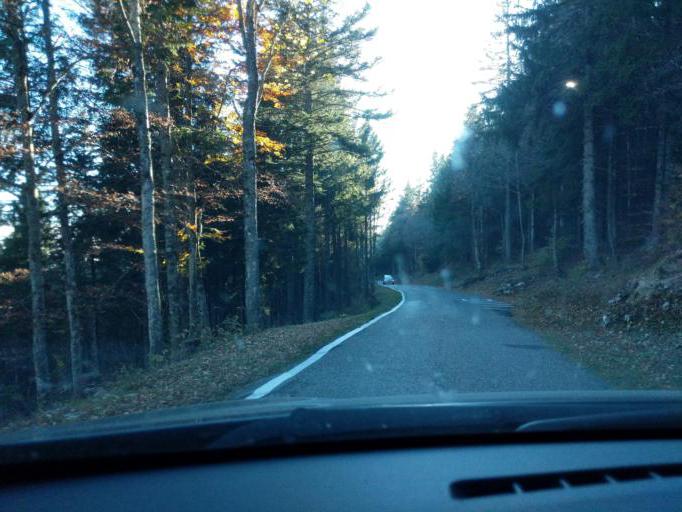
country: CH
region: Bern
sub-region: Jura bernois
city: Saint-Imier
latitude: 47.1194
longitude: 7.0419
